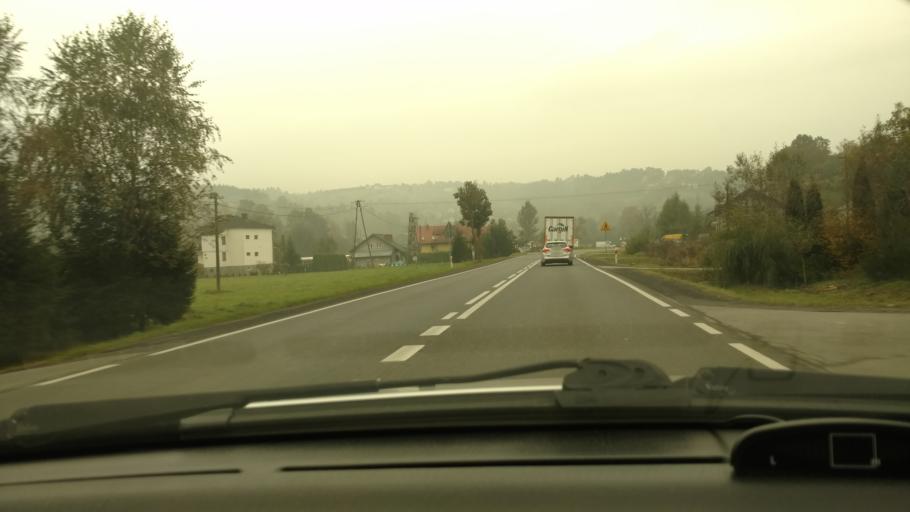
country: PL
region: Lesser Poland Voivodeship
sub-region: Powiat nowosadecki
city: Nawojowa
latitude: 49.6090
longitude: 20.7641
